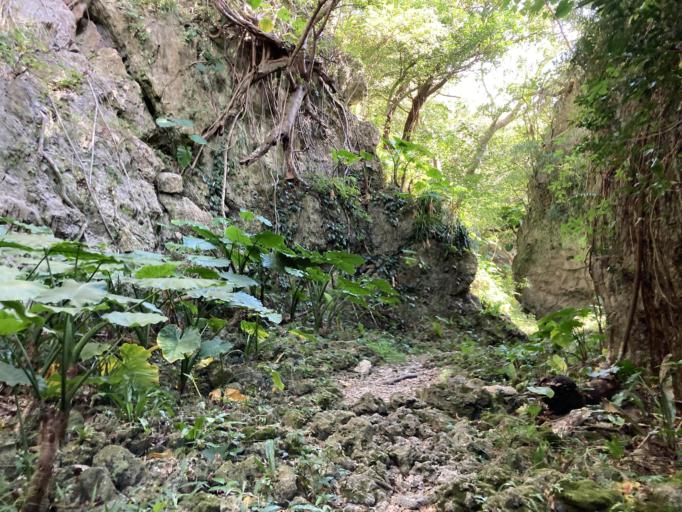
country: JP
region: Okinawa
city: Tomigusuku
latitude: 26.1440
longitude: 127.7803
